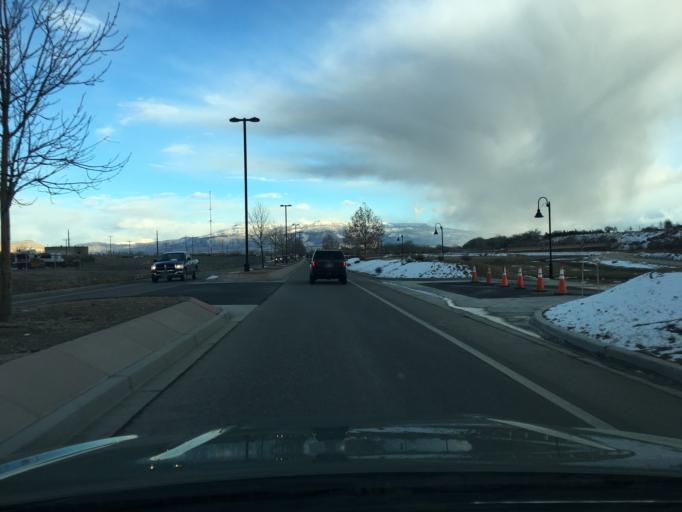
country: US
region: Colorado
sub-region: Mesa County
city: Grand Junction
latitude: 39.0560
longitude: -108.5523
